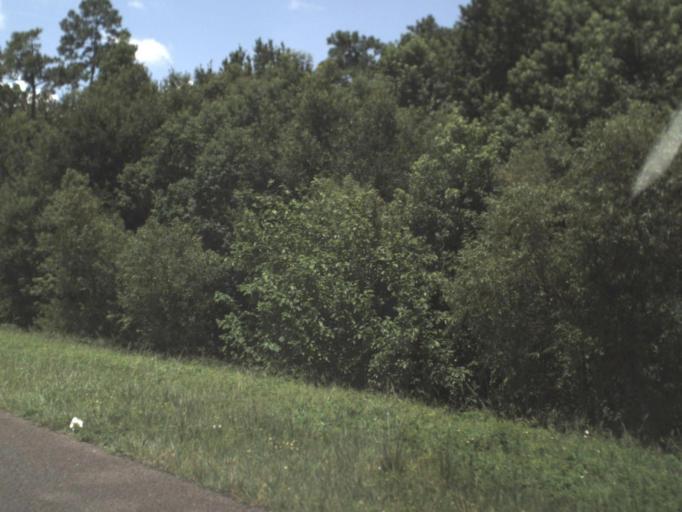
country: US
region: Florida
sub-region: Hernando County
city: Brooksville
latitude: 28.5417
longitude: -82.3705
